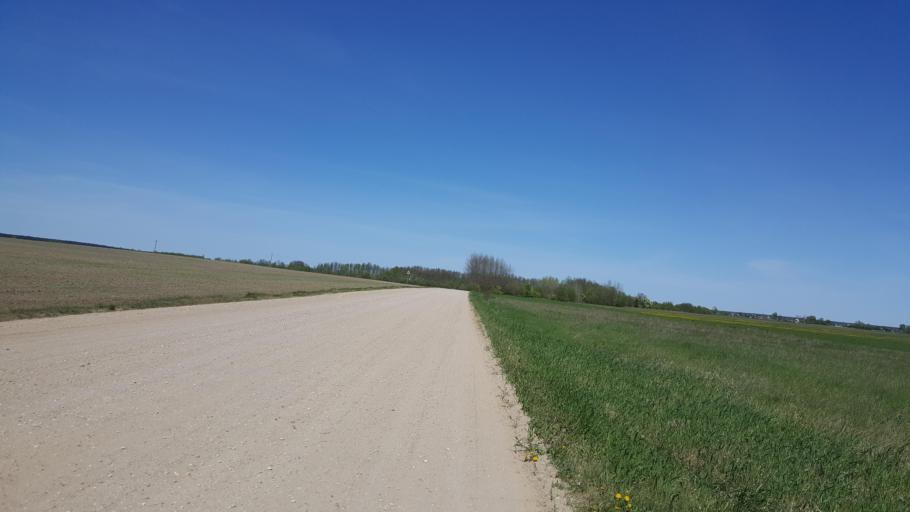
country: BY
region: Brest
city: Kamyanyets
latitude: 52.4468
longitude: 23.8640
